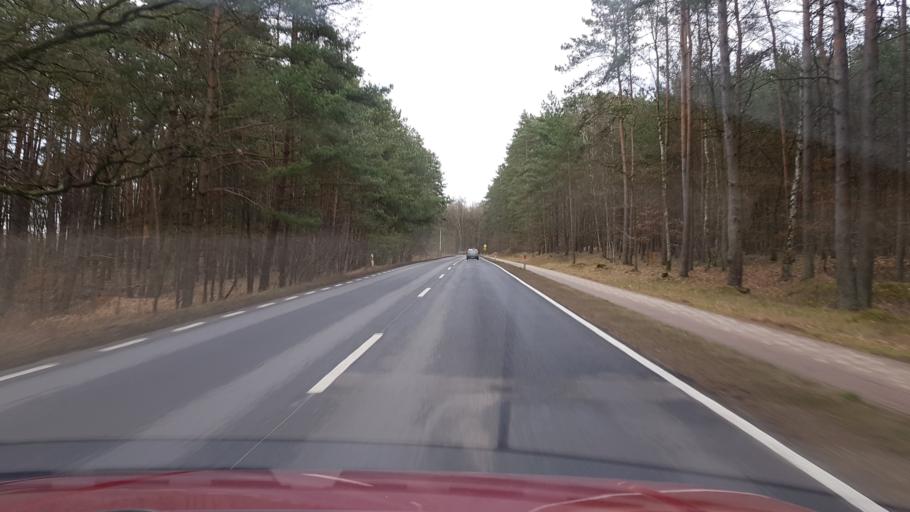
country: PL
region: West Pomeranian Voivodeship
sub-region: Powiat policki
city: Police
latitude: 53.5393
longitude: 14.4784
